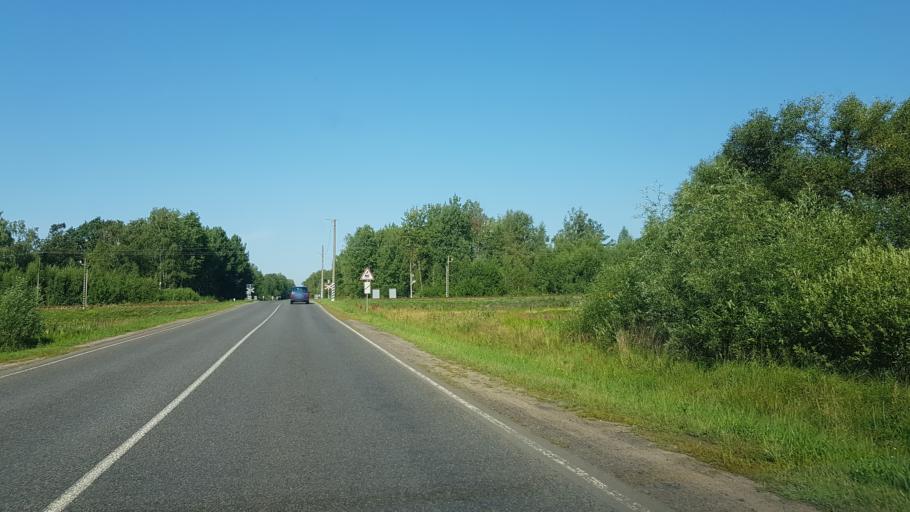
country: BY
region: Mogilev
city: Babruysk
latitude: 53.1070
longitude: 29.1756
